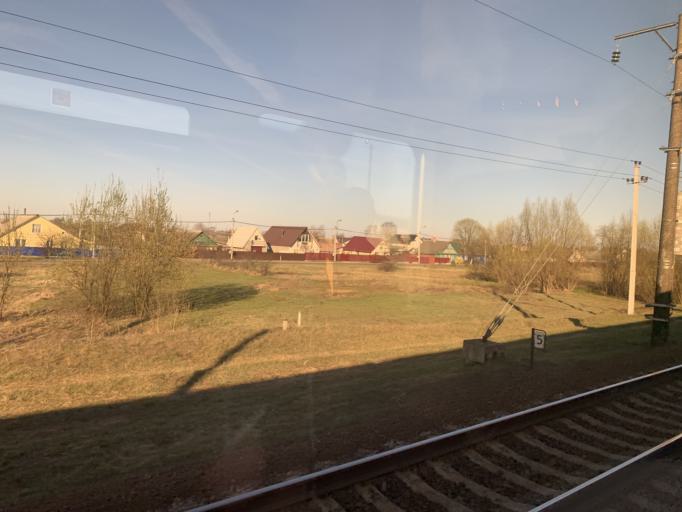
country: BY
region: Minsk
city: Maladzyechna
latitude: 54.3120
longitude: 26.8591
